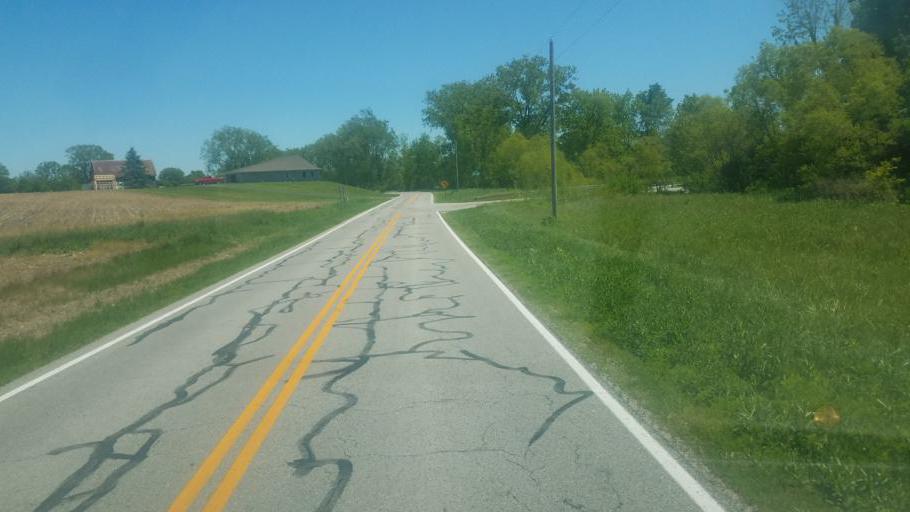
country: US
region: Ohio
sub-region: Miami County
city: Piqua
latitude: 40.2092
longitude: -84.2767
